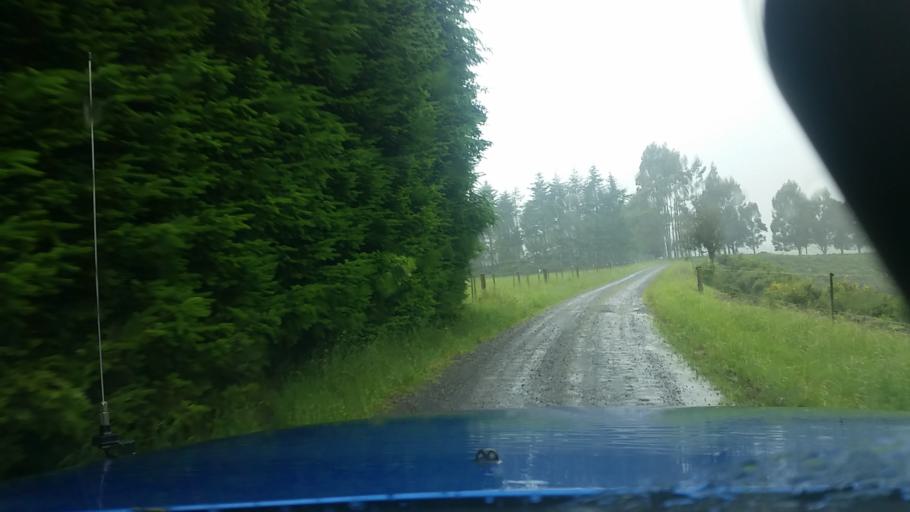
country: NZ
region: Canterbury
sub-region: Ashburton District
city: Methven
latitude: -43.5730
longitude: 171.5244
